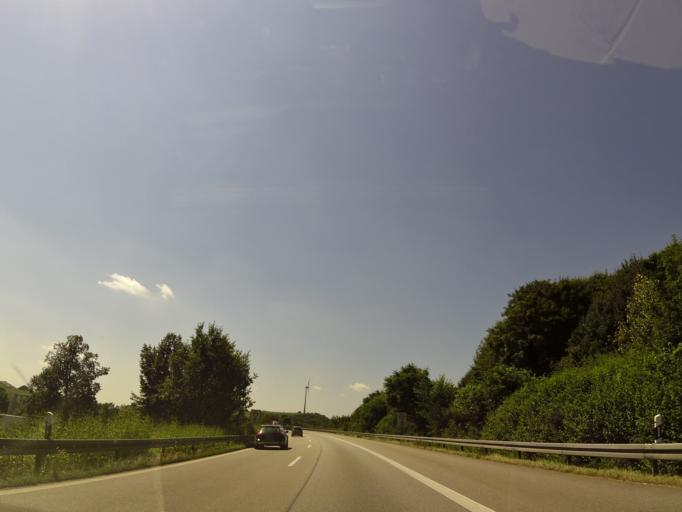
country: DE
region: Bavaria
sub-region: Upper Bavaria
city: Garching bei Munchen
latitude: 48.2261
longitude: 11.6306
